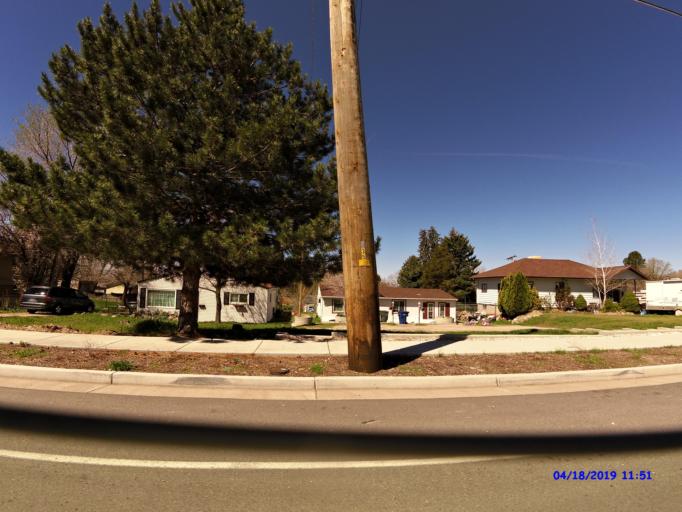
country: US
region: Utah
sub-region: Weber County
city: Ogden
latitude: 41.2540
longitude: -111.9480
